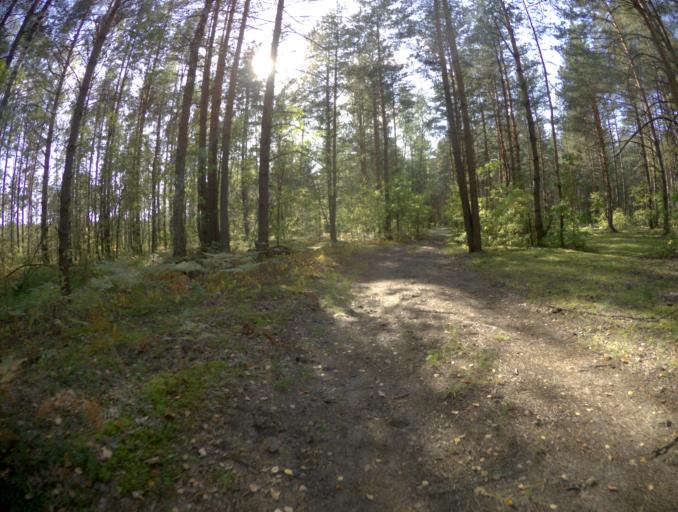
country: RU
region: Vladimir
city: Petushki
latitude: 55.8953
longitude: 39.4628
